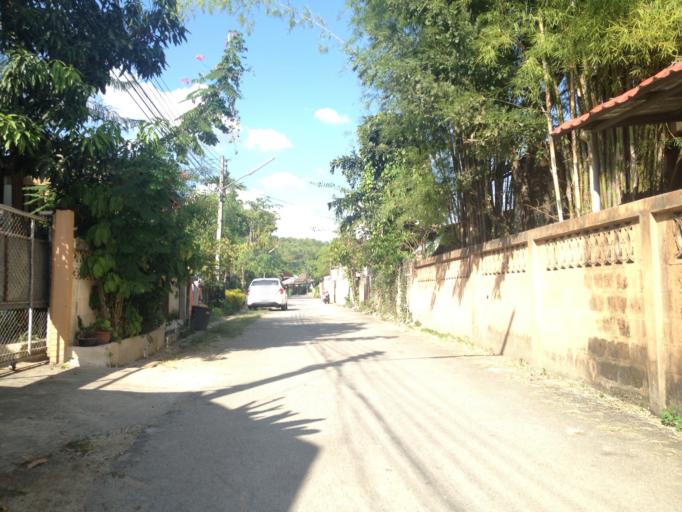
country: TH
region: Chiang Mai
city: Chiang Mai
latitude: 18.7689
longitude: 98.9413
